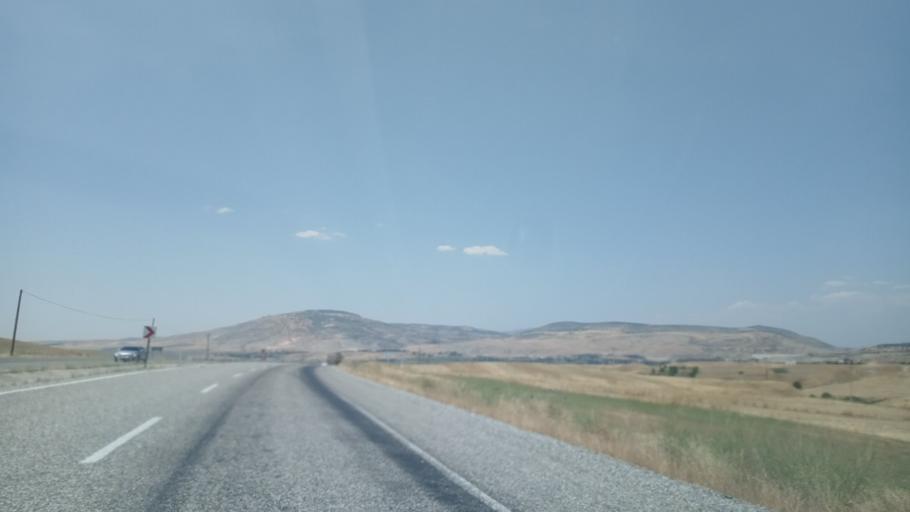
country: TR
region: Diyarbakir
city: Malabadi
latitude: 38.1339
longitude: 41.2439
